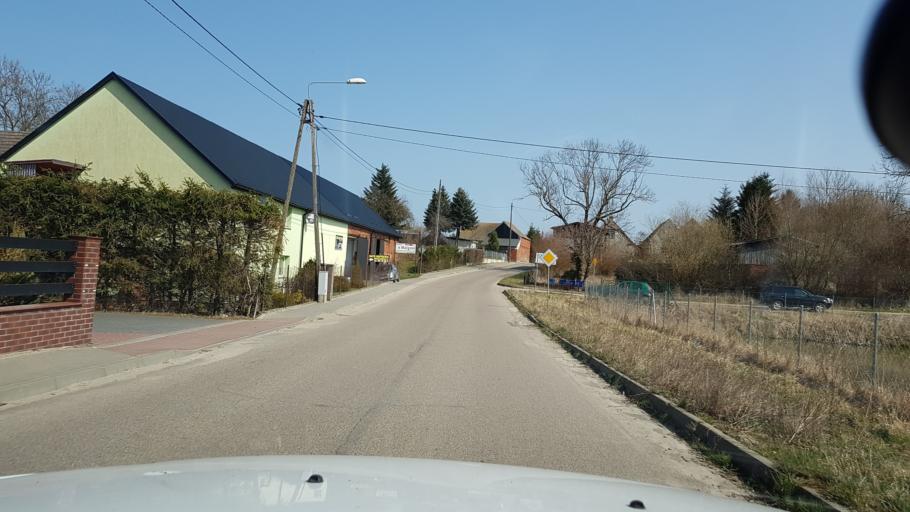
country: PL
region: West Pomeranian Voivodeship
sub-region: Powiat slawienski
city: Darlowo
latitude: 54.5120
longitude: 16.5128
